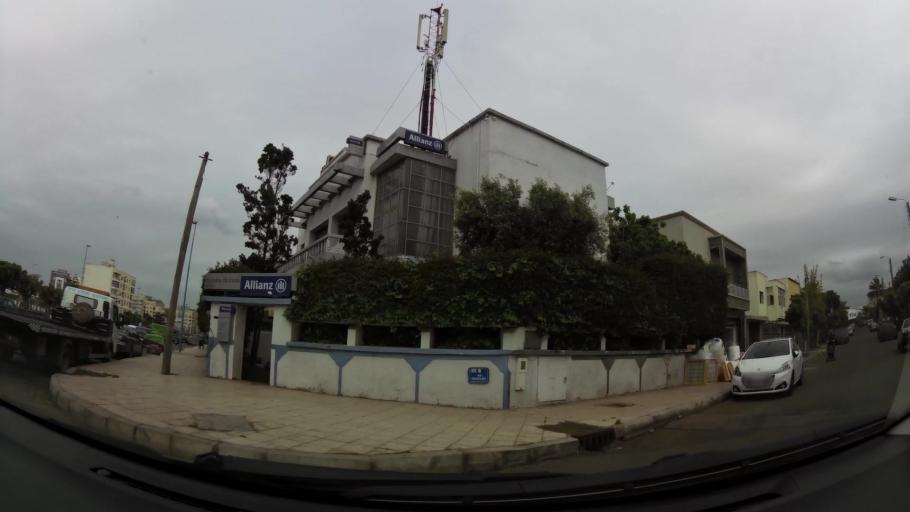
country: MA
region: Grand Casablanca
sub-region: Casablanca
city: Casablanca
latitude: 33.5956
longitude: -7.6494
